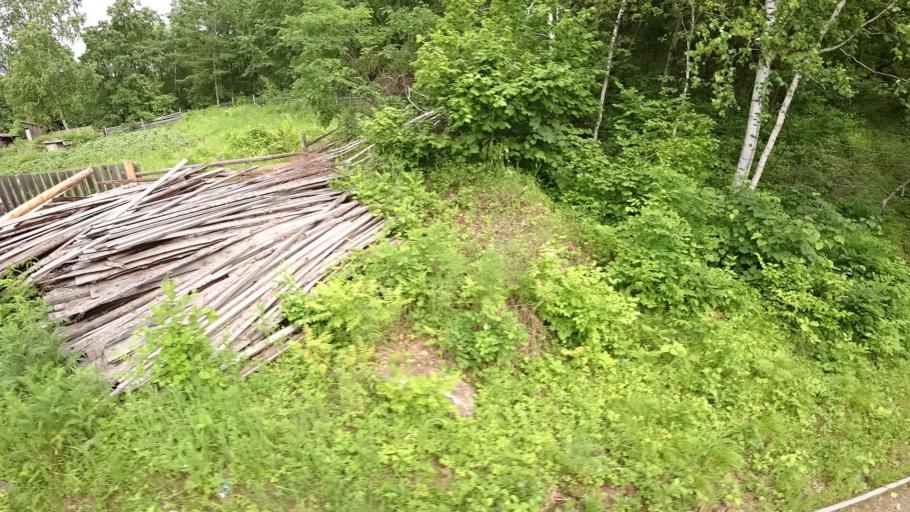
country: RU
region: Khabarovsk Krai
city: Litovko
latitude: 49.3625
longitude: 135.1744
